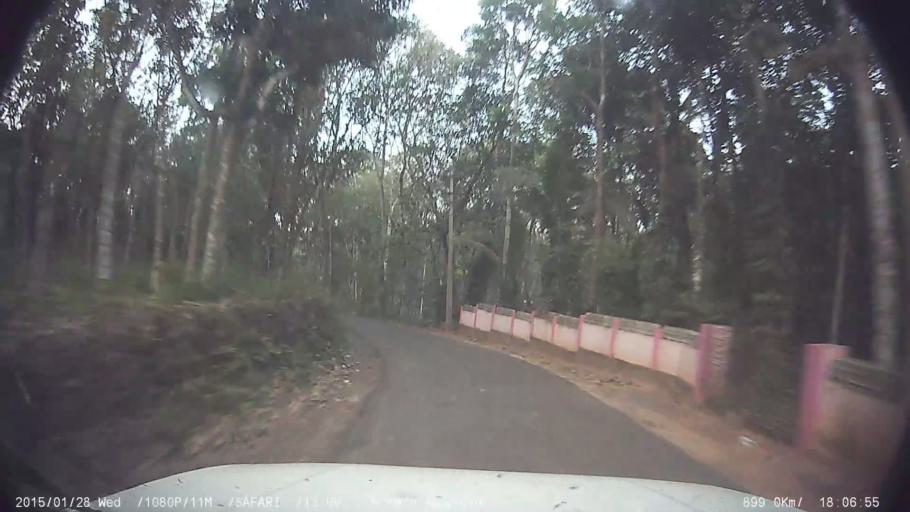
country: IN
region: Kerala
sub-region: Kottayam
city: Palackattumala
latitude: 9.7317
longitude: 76.5767
